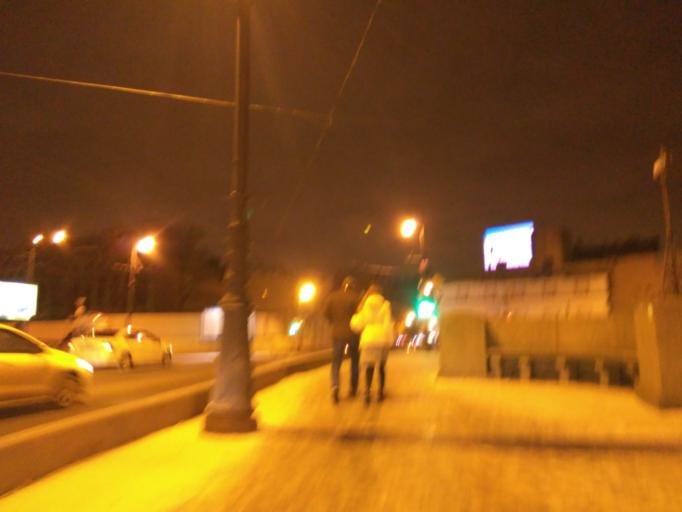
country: RU
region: St.-Petersburg
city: Petrogradka
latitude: 59.9697
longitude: 30.3082
